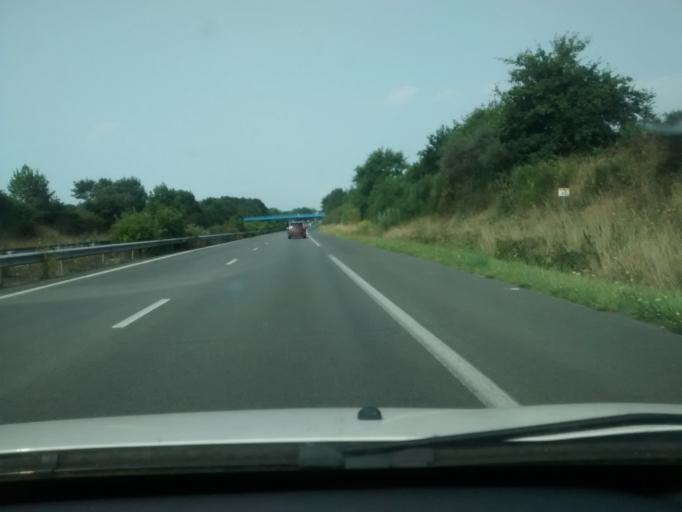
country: FR
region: Pays de la Loire
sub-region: Departement de la Loire-Atlantique
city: Saint-Andre-des-Eaux
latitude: 47.2839
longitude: -2.2901
